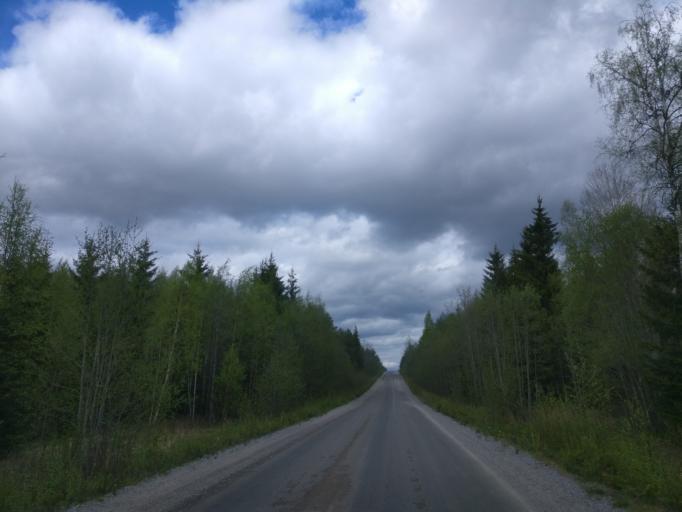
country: SE
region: Gaevleborg
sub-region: Soderhamns Kommun
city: Soderhamn
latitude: 61.4289
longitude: 16.9950
